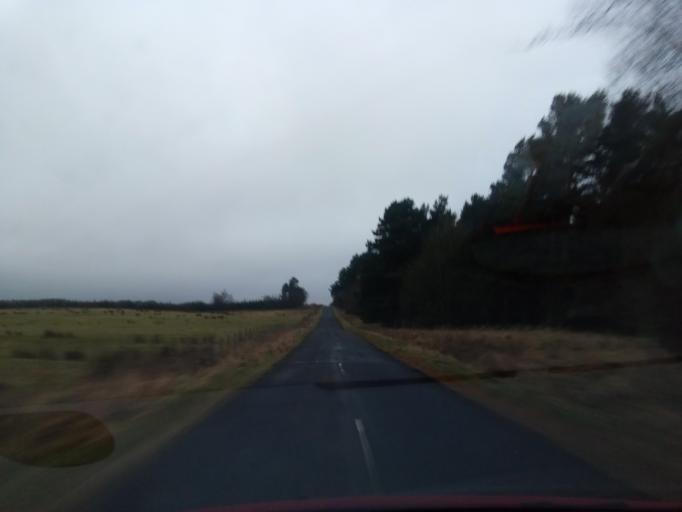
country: GB
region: England
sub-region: Northumberland
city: Rothley
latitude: 55.2031
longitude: -2.0029
